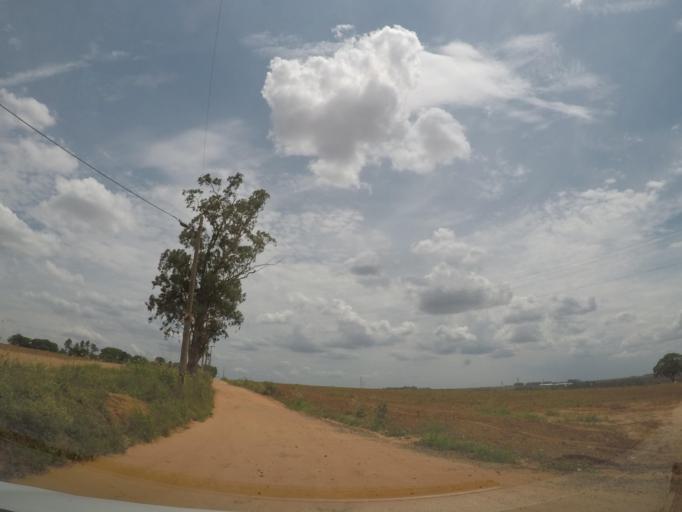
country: BR
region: Sao Paulo
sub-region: Sumare
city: Sumare
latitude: -22.8350
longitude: -47.2908
